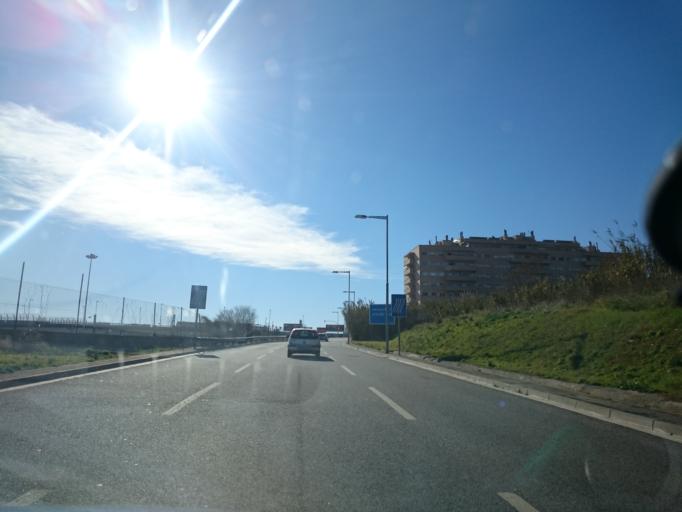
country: ES
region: Catalonia
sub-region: Provincia de Barcelona
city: Sant Andreu de Palomar
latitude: 41.4443
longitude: 2.1944
